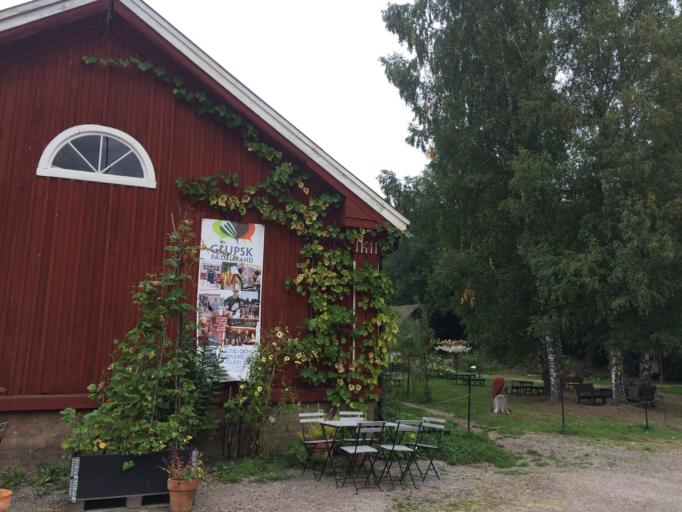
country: SE
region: Vaestra Goetaland
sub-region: Bengtsfors Kommun
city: Dals Langed
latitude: 58.9952
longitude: 12.4689
